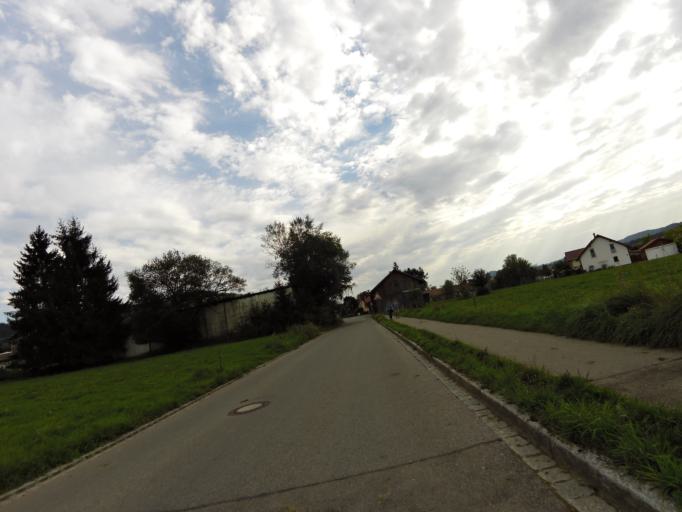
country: DE
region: Bavaria
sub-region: Swabia
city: Weiler-Simmerberg
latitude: 47.5872
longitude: 9.9189
